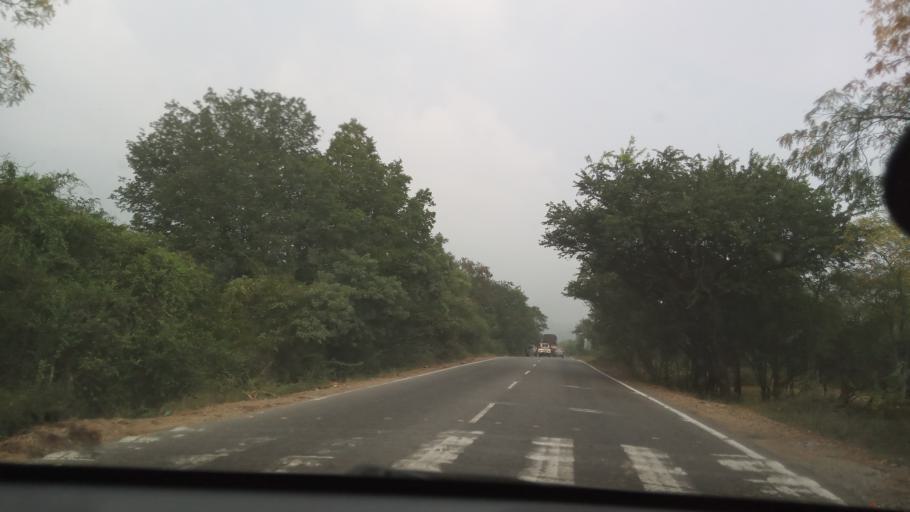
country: IN
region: Tamil Nadu
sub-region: Erode
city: Sathyamangalam
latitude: 11.5701
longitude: 77.1348
